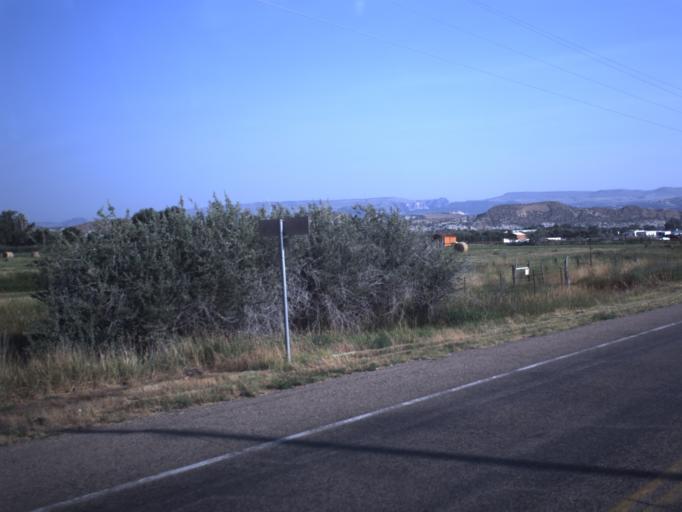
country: US
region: Utah
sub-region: Uintah County
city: Vernal
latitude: 40.4751
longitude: -109.5288
